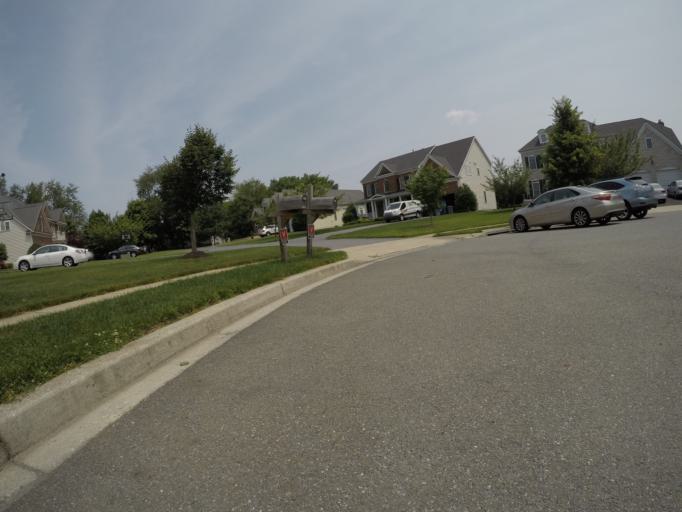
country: US
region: Maryland
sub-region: Howard County
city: Columbia
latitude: 39.2409
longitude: -76.8184
